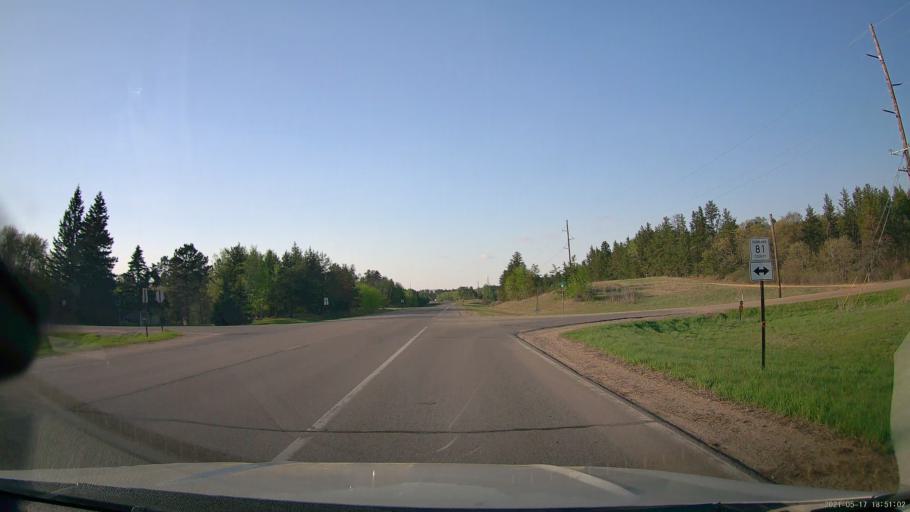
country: US
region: Minnesota
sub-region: Hubbard County
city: Park Rapids
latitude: 46.9433
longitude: -95.0163
